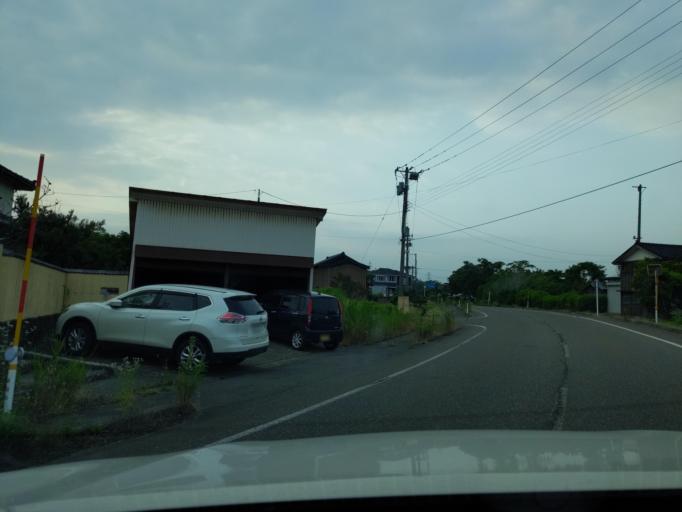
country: JP
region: Niigata
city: Kashiwazaki
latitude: 37.4026
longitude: 138.6001
